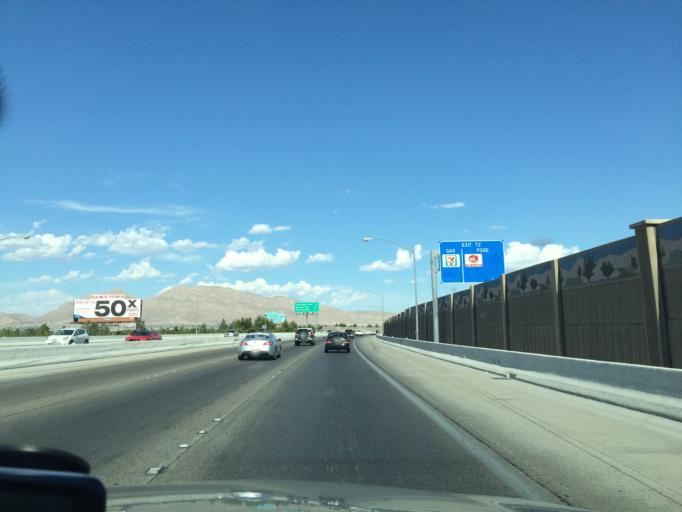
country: US
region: Nevada
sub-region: Clark County
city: North Las Vegas
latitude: 36.1675
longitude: -115.1029
